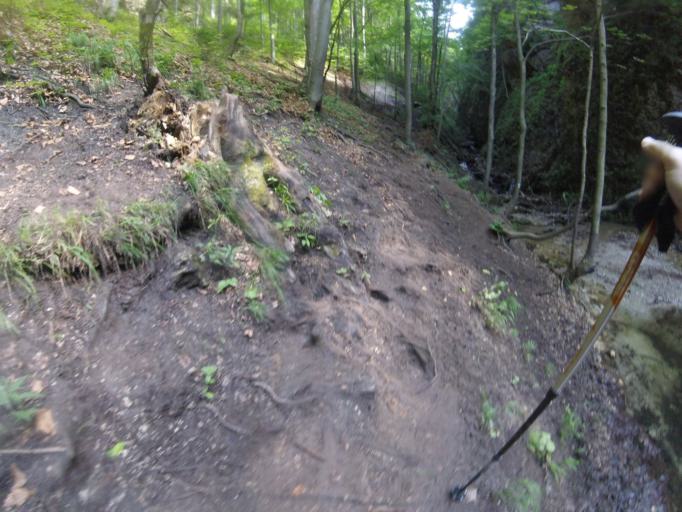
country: SK
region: Zilinsky
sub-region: Okres Zilina
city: Terchova
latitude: 49.2415
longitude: 19.0844
